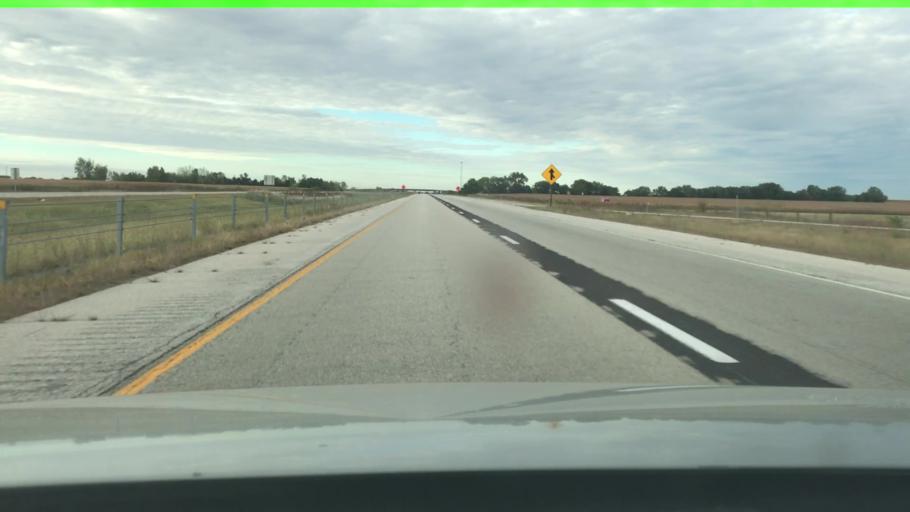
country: US
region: Illinois
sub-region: Livingston County
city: Odell
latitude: 41.0035
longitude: -88.5375
